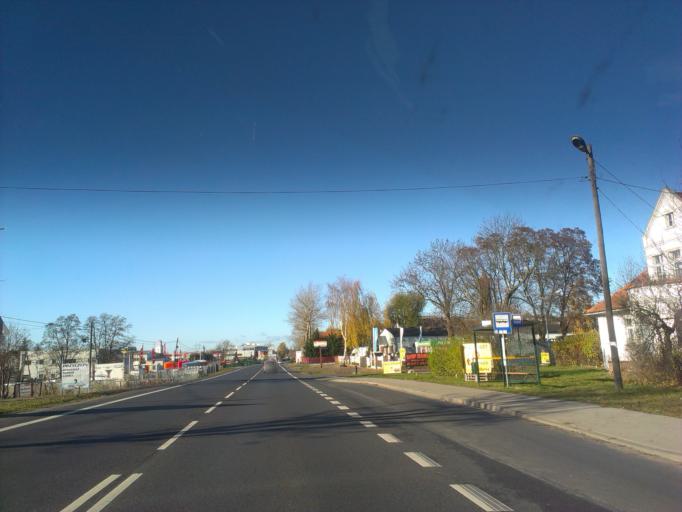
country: PL
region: Greater Poland Voivodeship
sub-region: Powiat poznanski
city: Zlotniki
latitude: 52.4831
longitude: 16.8594
